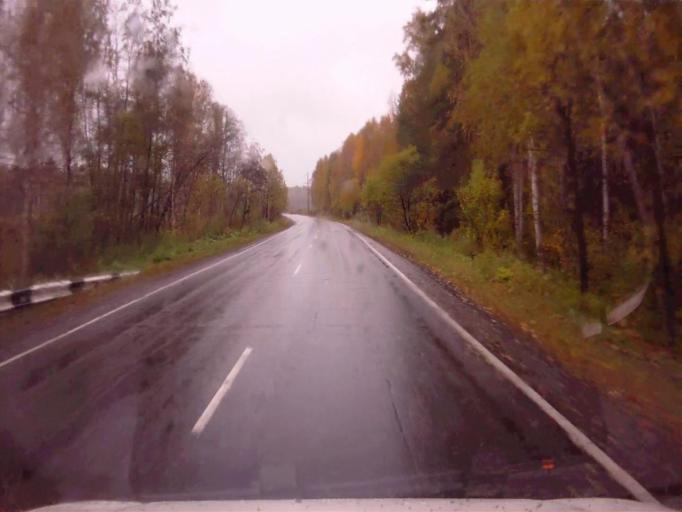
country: RU
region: Chelyabinsk
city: Verkhniy Ufaley
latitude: 55.9427
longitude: 60.4084
